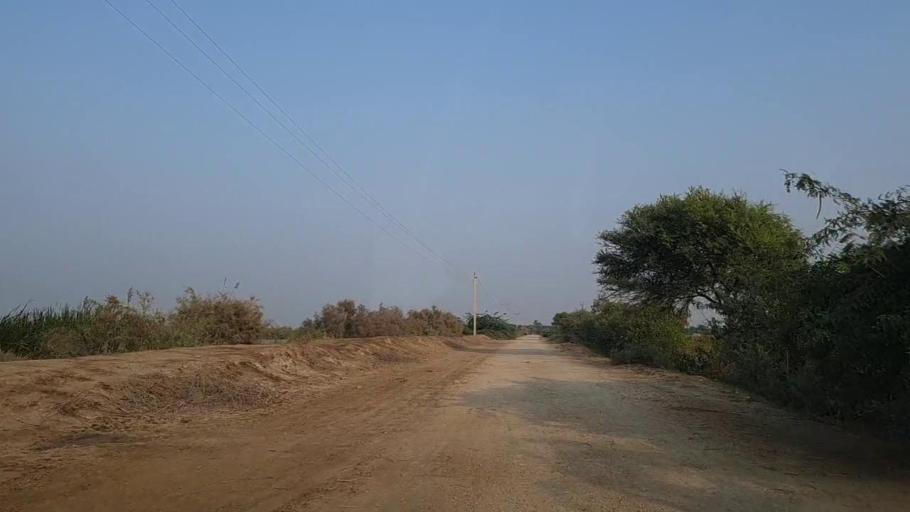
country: PK
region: Sindh
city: Thatta
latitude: 24.6921
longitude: 67.8044
